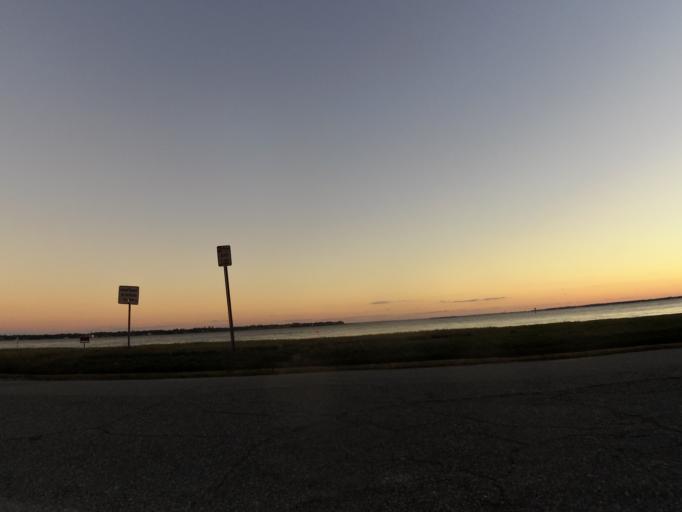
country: US
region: Florida
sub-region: Duval County
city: Jacksonville
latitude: 30.3102
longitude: -81.6782
